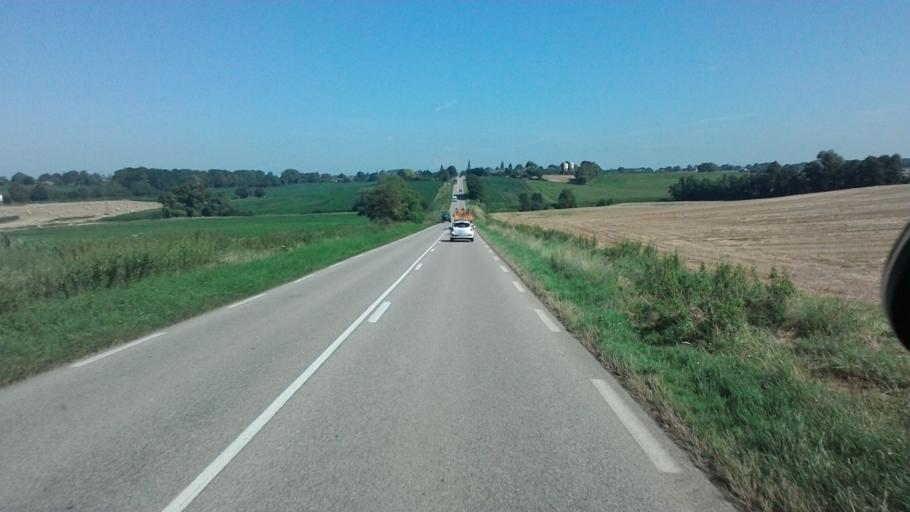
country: FR
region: Rhone-Alpes
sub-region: Departement de l'Ain
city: Saint-Trivier-de-Courtes
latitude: 46.4464
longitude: 5.0887
